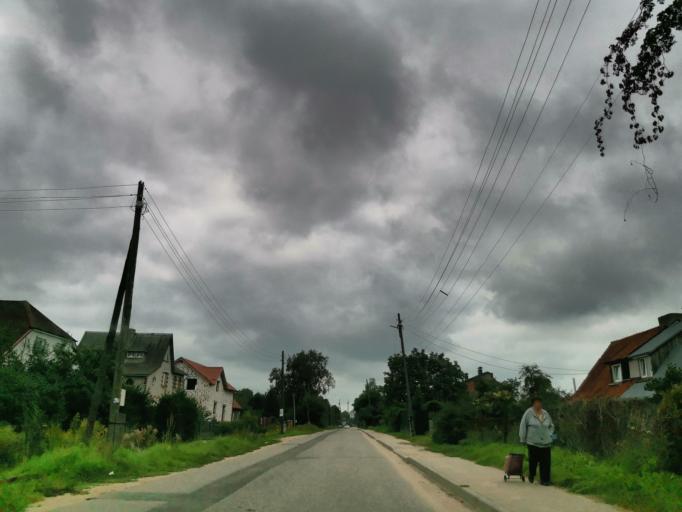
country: RU
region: Kaliningrad
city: Chernyakhovsk
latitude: 54.6539
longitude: 21.8367
